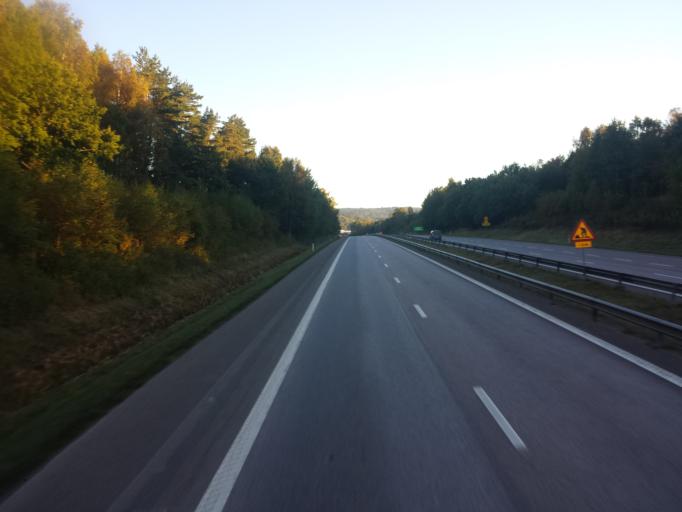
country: SE
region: Halland
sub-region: Kungsbacka Kommun
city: Kungsbacka
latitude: 57.4926
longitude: 12.0480
